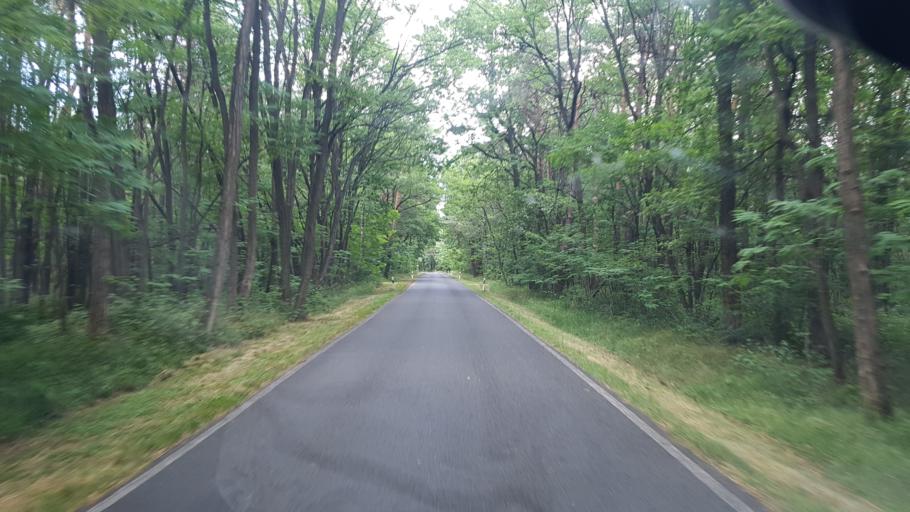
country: DE
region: Brandenburg
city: Sallgast
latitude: 51.5805
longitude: 13.9146
